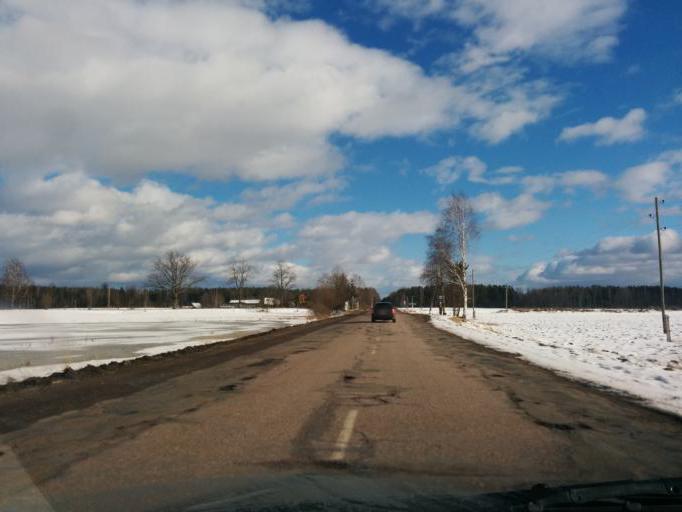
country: LV
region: Gulbenes Rajons
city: Gulbene
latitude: 57.1913
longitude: 26.9050
